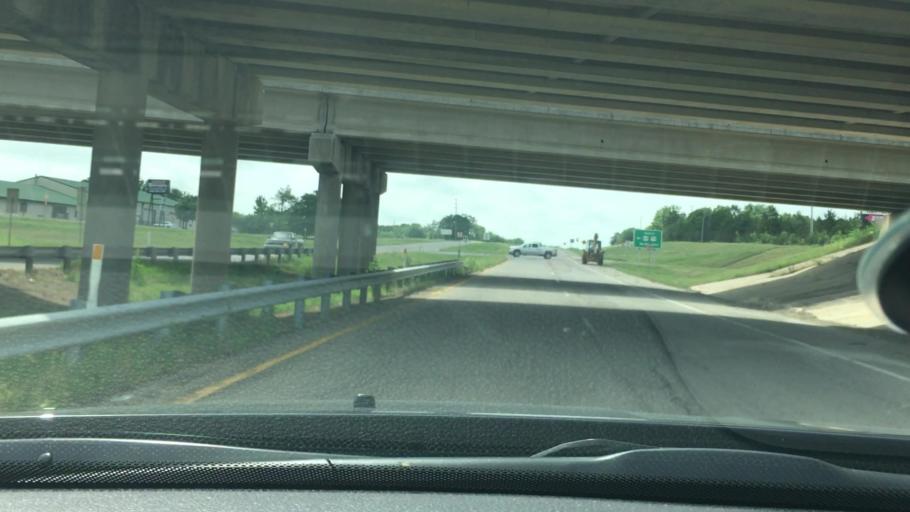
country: US
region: Oklahoma
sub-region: Bryan County
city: Durant
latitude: 34.0379
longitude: -96.3752
